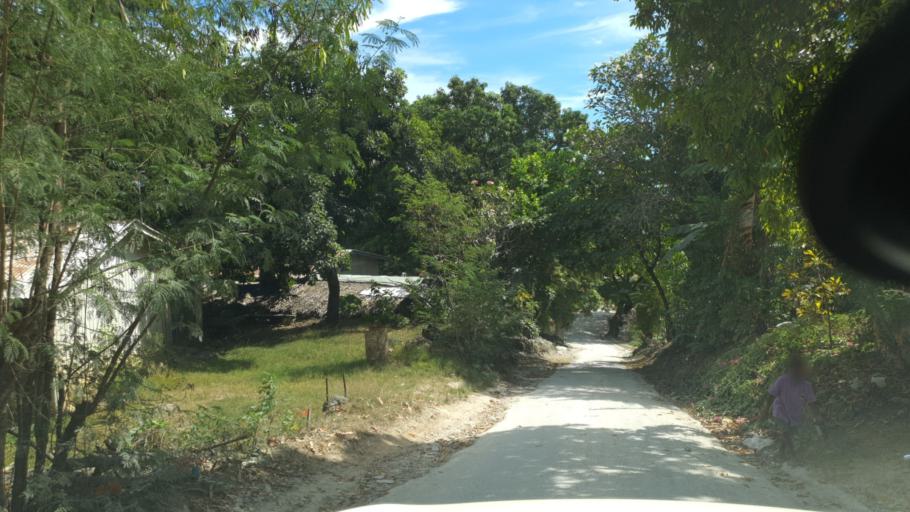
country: SB
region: Guadalcanal
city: Honiara
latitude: -9.4353
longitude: 159.9806
